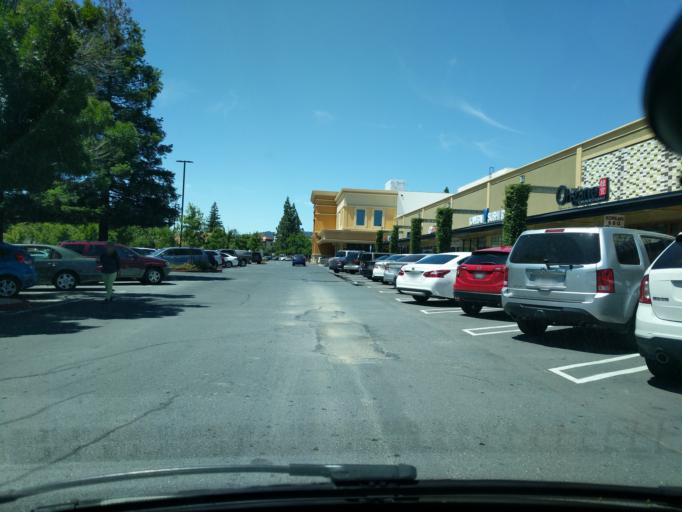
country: US
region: California
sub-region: Contra Costa County
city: Concord
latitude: 37.9730
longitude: -122.0430
